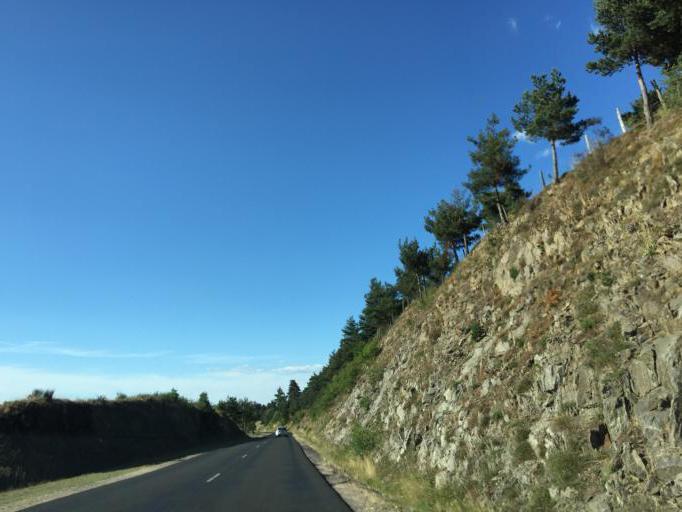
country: FR
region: Auvergne
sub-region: Departement de la Haute-Loire
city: Saugues
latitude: 44.9737
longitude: 3.6134
